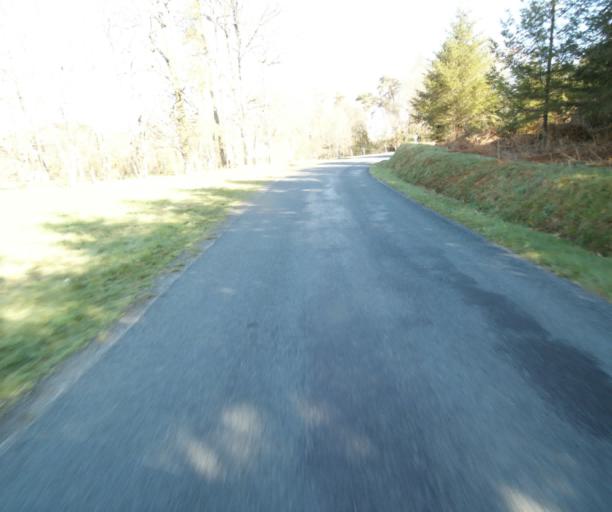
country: FR
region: Limousin
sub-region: Departement de la Correze
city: Correze
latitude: 45.2888
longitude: 1.8702
